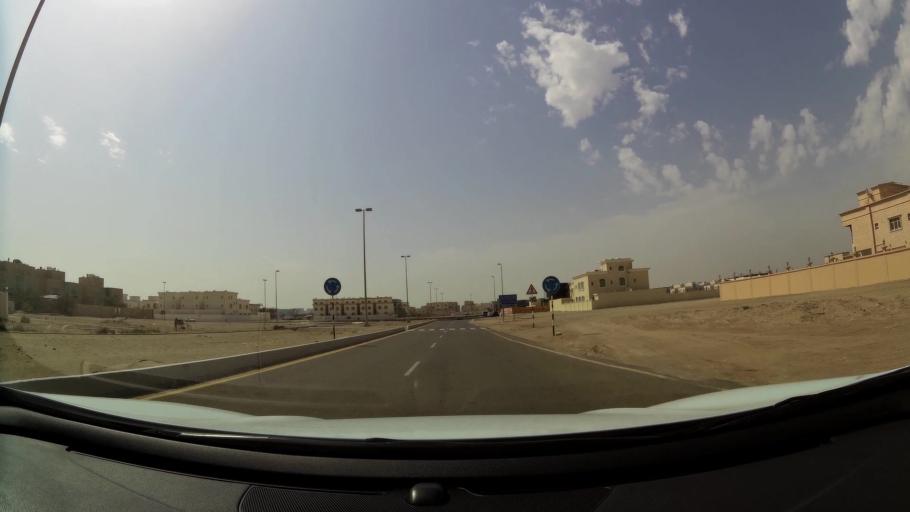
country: AE
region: Abu Dhabi
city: Abu Dhabi
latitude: 24.3321
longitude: 54.5529
